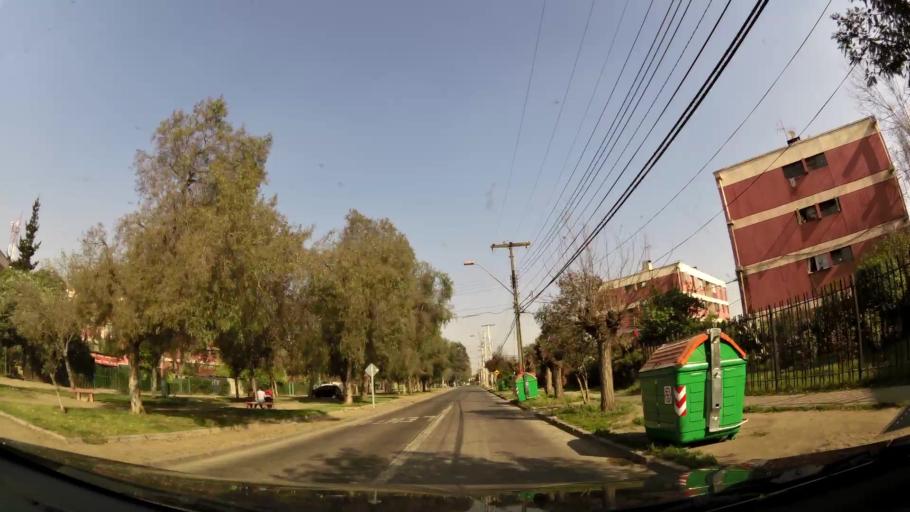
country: CL
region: Santiago Metropolitan
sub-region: Provincia de Santiago
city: Lo Prado
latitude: -33.3718
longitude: -70.6855
